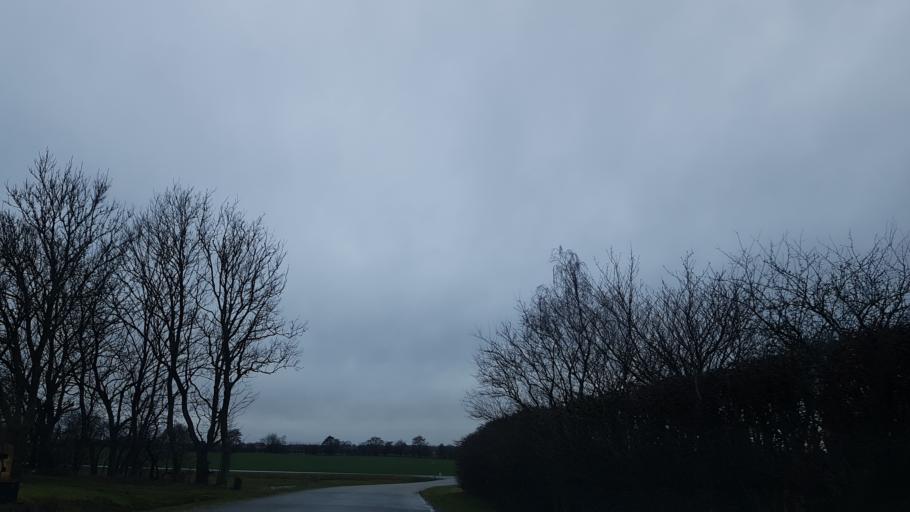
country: DK
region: South Denmark
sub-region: Kolding Kommune
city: Vamdrup
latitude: 55.3838
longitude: 9.2968
